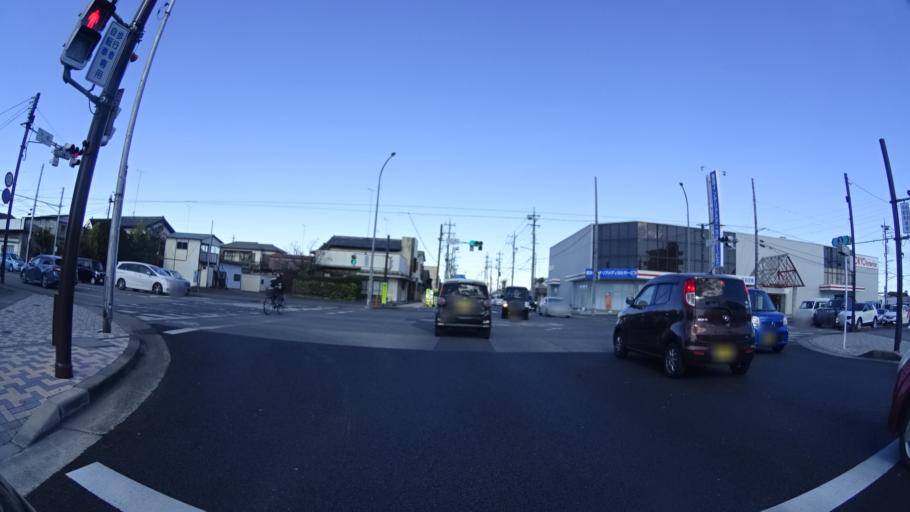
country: JP
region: Tochigi
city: Tochigi
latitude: 36.3942
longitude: 139.7370
